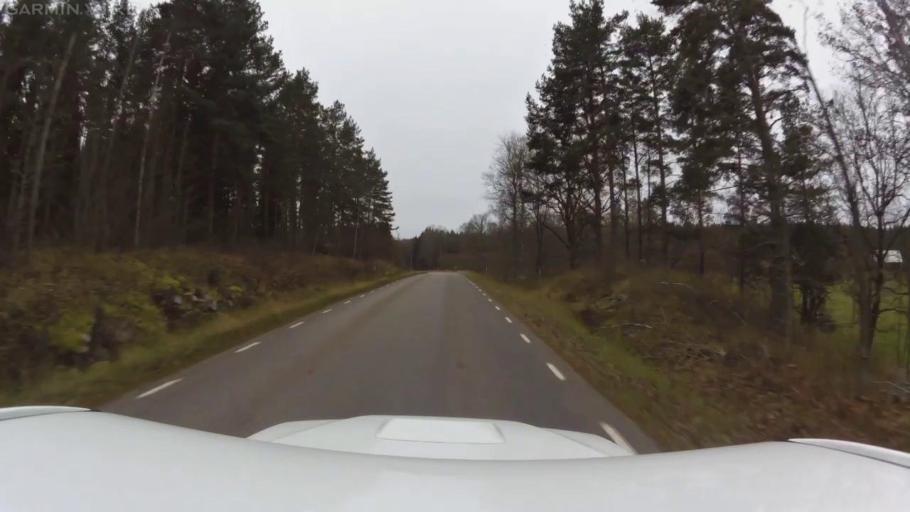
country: SE
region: OEstergoetland
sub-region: Linkopings Kommun
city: Vikingstad
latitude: 58.2599
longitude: 15.3847
